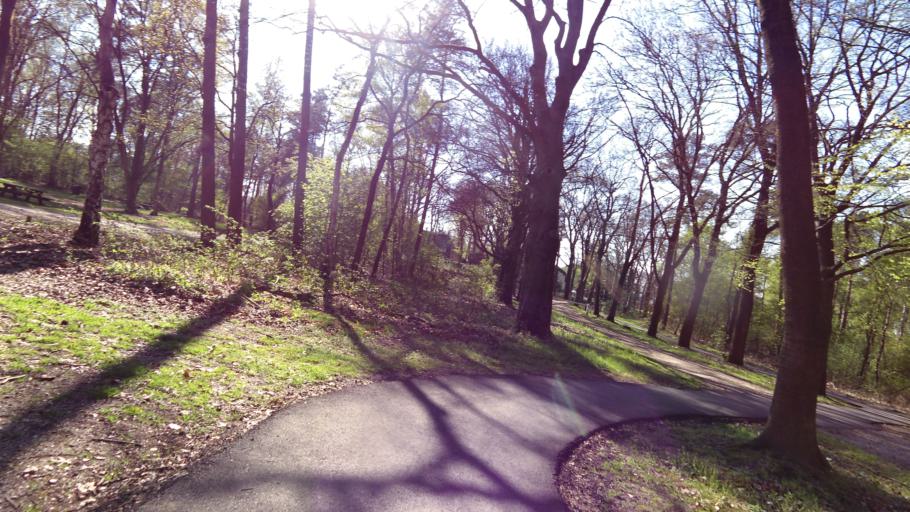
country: NL
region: Gelderland
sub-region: Gemeente Arnhem
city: Hoogkamp
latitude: 52.0147
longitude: 5.8776
